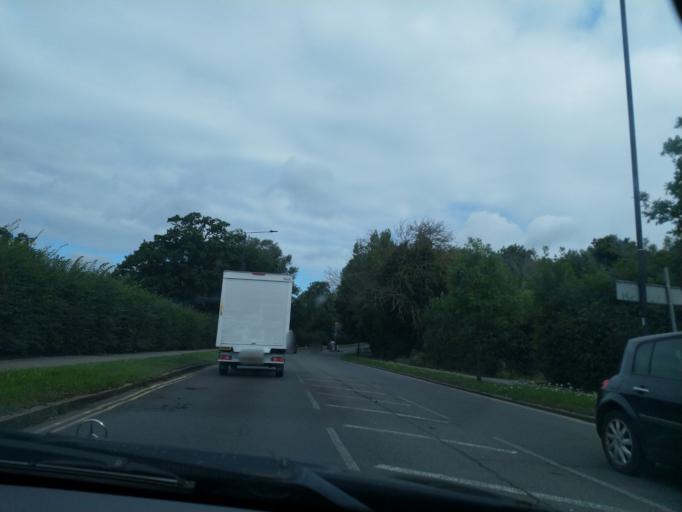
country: GB
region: England
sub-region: Greater London
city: Harrow on the Hill
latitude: 51.5727
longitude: -0.3244
